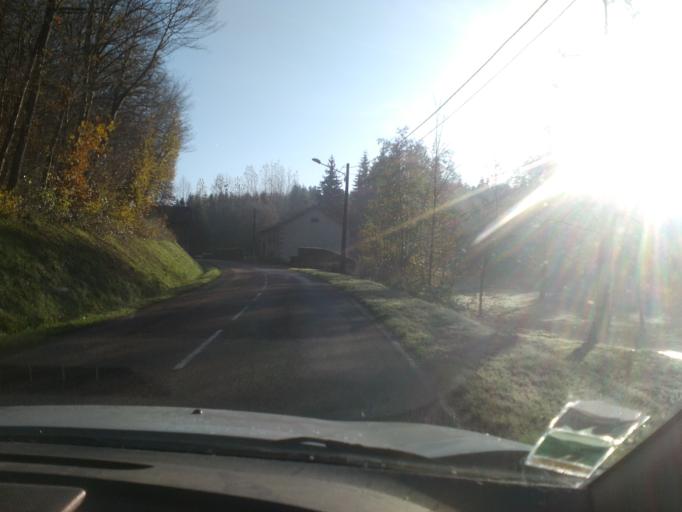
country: FR
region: Lorraine
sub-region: Departement des Vosges
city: Uzemain
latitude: 48.0646
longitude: 6.3232
